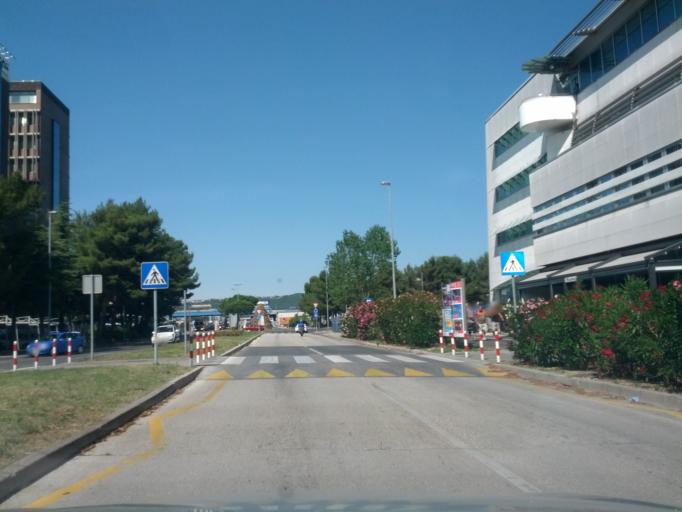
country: SI
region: Koper-Capodistria
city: Koper
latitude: 45.5472
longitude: 13.7378
